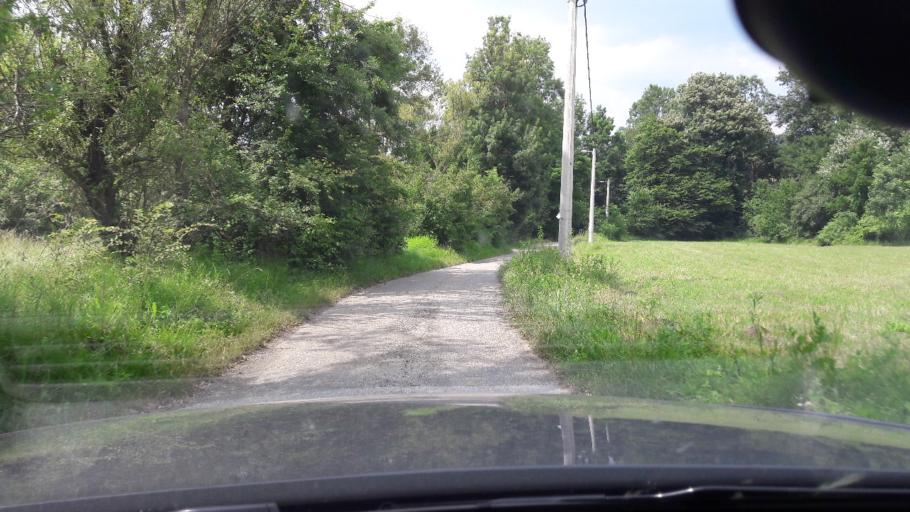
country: RS
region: Central Serbia
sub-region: Belgrade
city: Sopot
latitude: 44.6239
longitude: 20.5995
